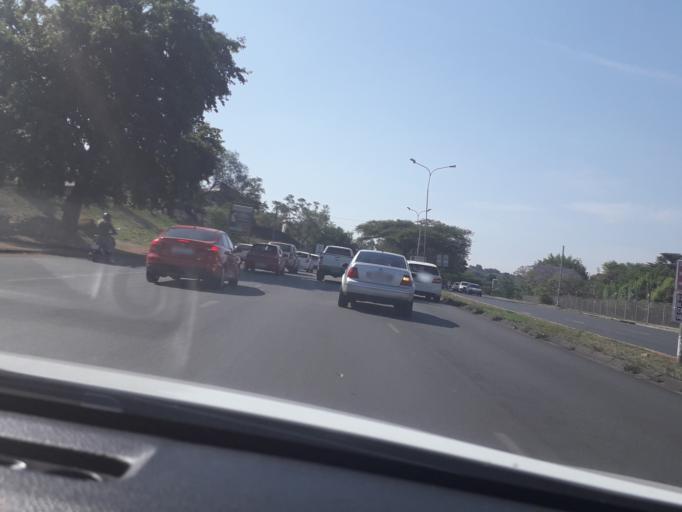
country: ZA
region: Gauteng
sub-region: City of Johannesburg Metropolitan Municipality
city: Johannesburg
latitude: -26.0893
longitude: 28.0253
